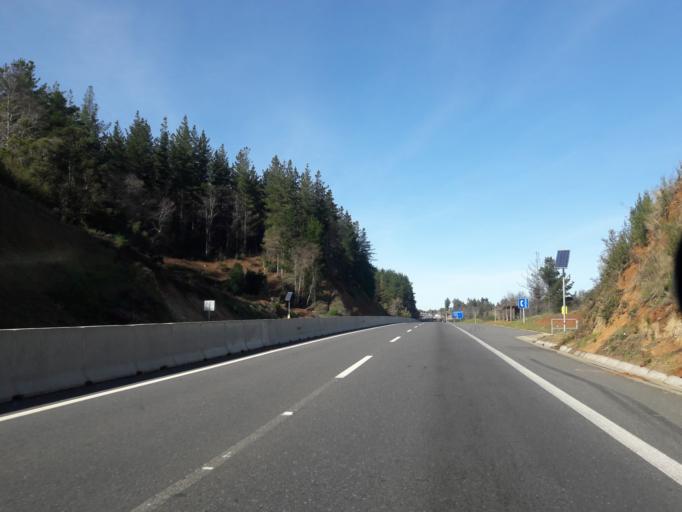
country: CL
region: Biobio
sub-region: Provincia de Concepcion
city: Chiguayante
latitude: -36.9255
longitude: -72.7707
